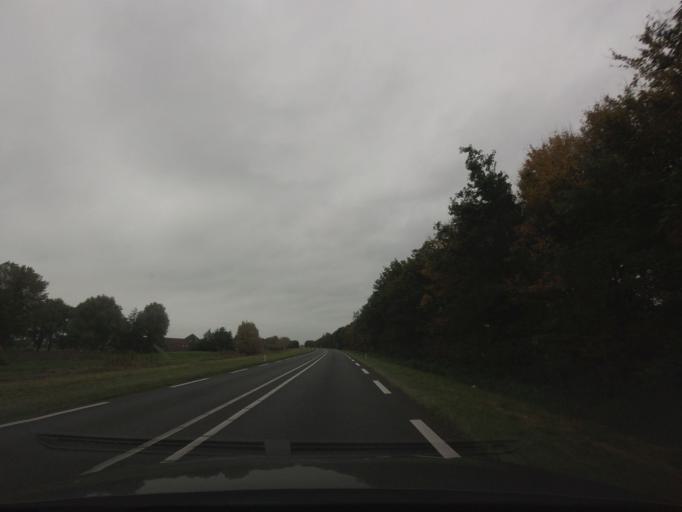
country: NL
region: North Holland
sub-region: Gemeente Alkmaar
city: Alkmaar
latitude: 52.6559
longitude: 4.7398
